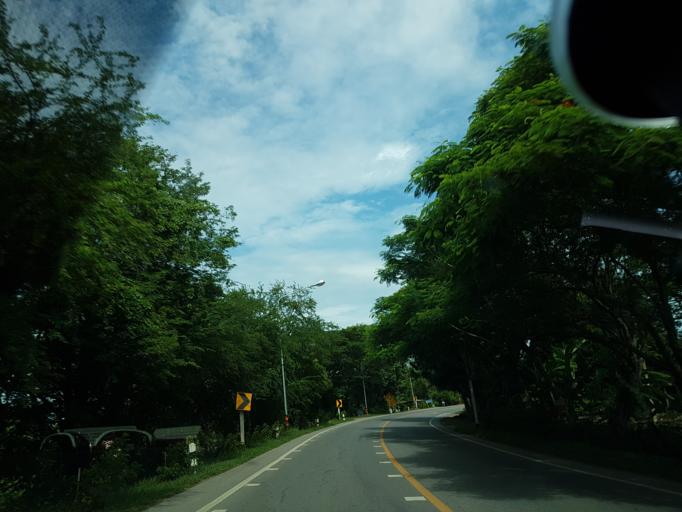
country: TH
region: Ang Thong
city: Chaiyo
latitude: 14.7213
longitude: 100.4968
